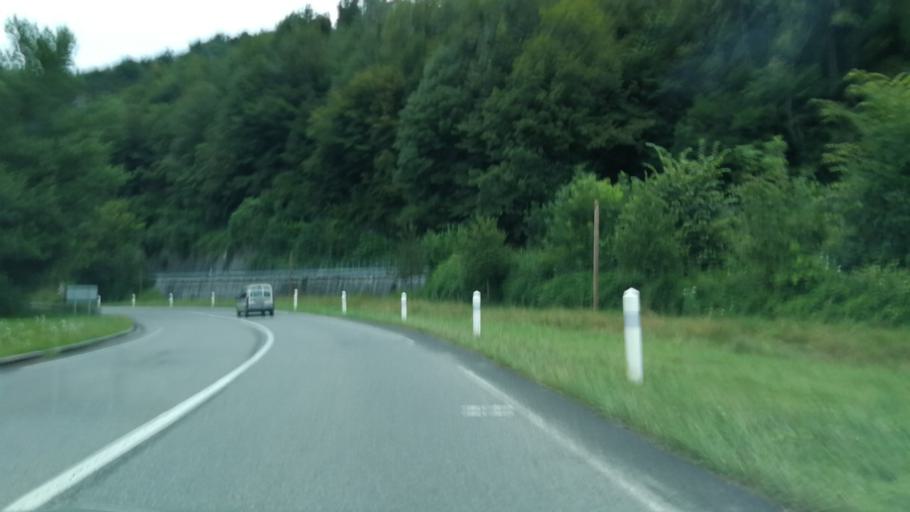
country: FR
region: Aquitaine
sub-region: Departement des Pyrenees-Atlantiques
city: Arette
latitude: 43.0112
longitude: -0.6028
